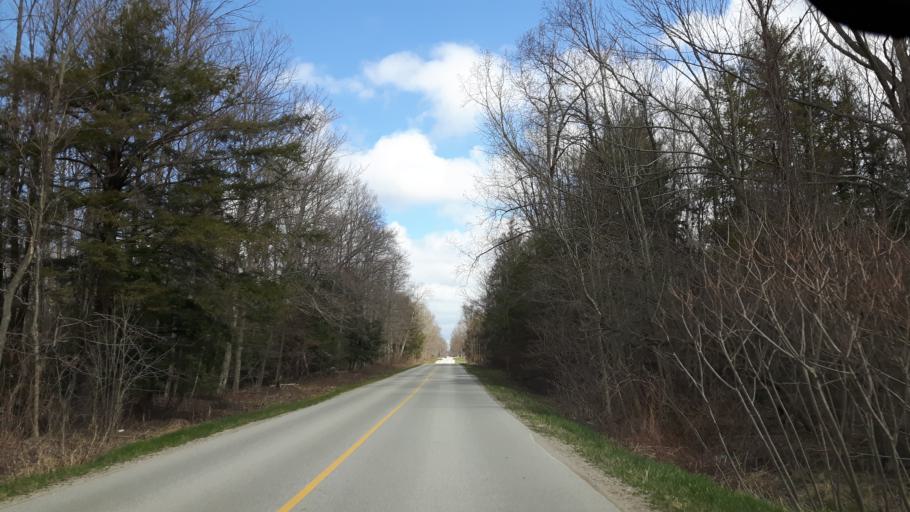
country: CA
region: Ontario
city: Goderich
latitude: 43.6179
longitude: -81.6846
